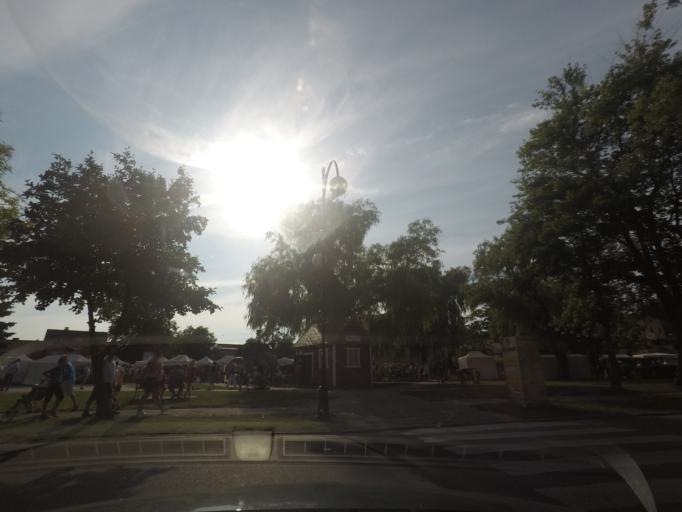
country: PL
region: Pomeranian Voivodeship
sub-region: Powiat leborski
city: Leba
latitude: 54.7610
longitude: 17.5552
